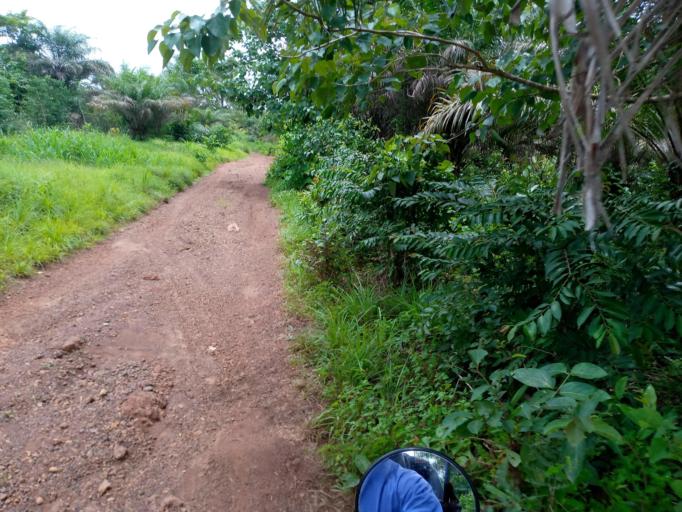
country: SL
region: Northern Province
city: Mange
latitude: 8.9895
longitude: -12.7884
